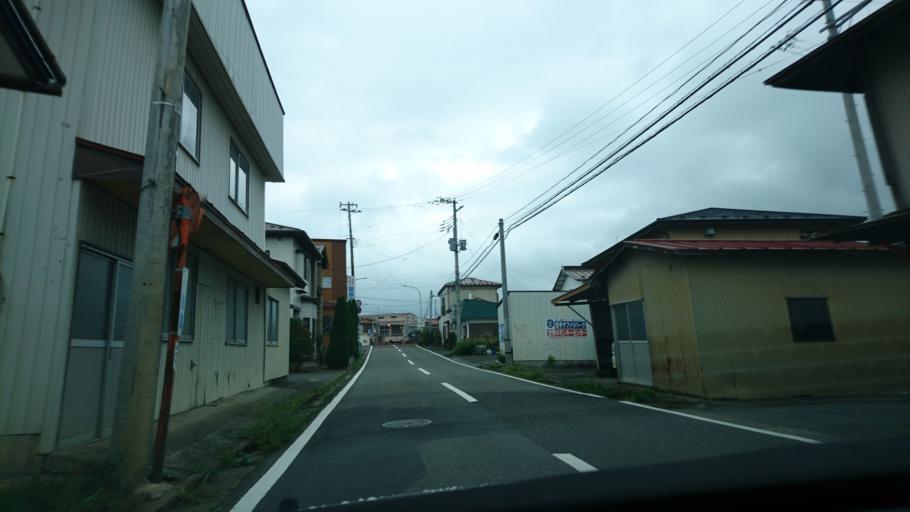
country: JP
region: Iwate
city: Ichinoseki
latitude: 38.8080
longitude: 140.9487
